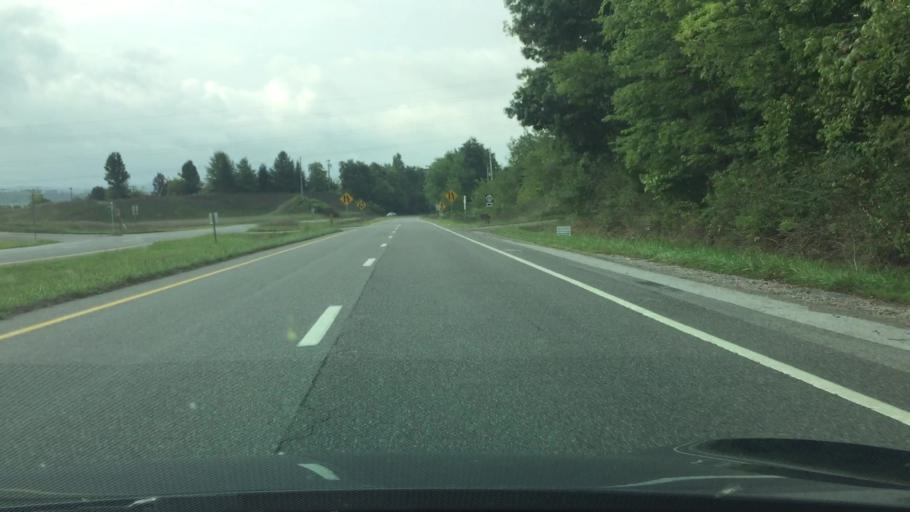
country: US
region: Virginia
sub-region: City of Radford
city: Radford
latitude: 37.0942
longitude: -80.5071
